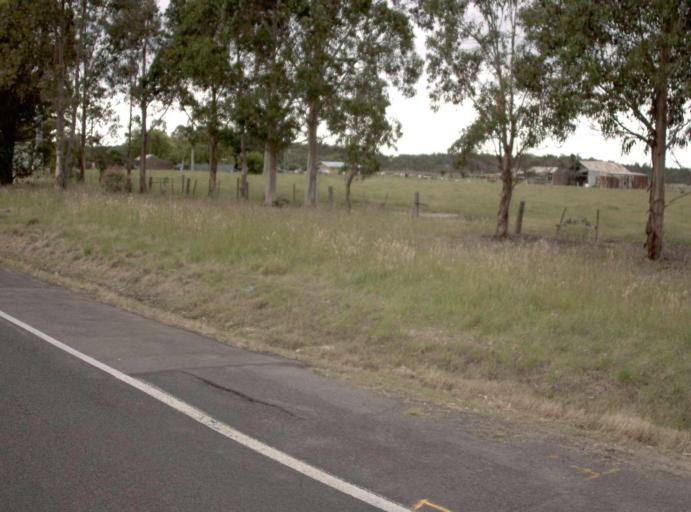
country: AU
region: Victoria
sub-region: Wellington
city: Sale
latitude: -38.2984
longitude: 147.0336
